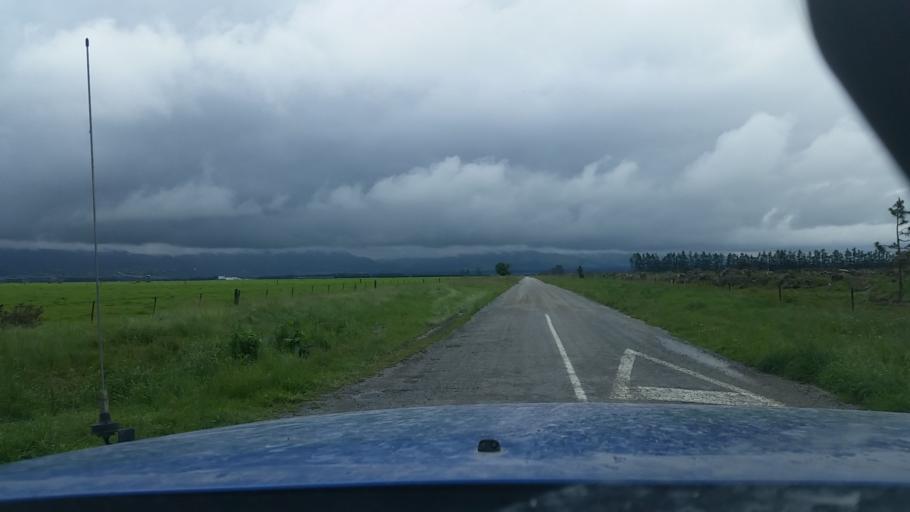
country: NZ
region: Canterbury
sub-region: Ashburton District
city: Methven
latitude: -43.7182
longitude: 171.4574
